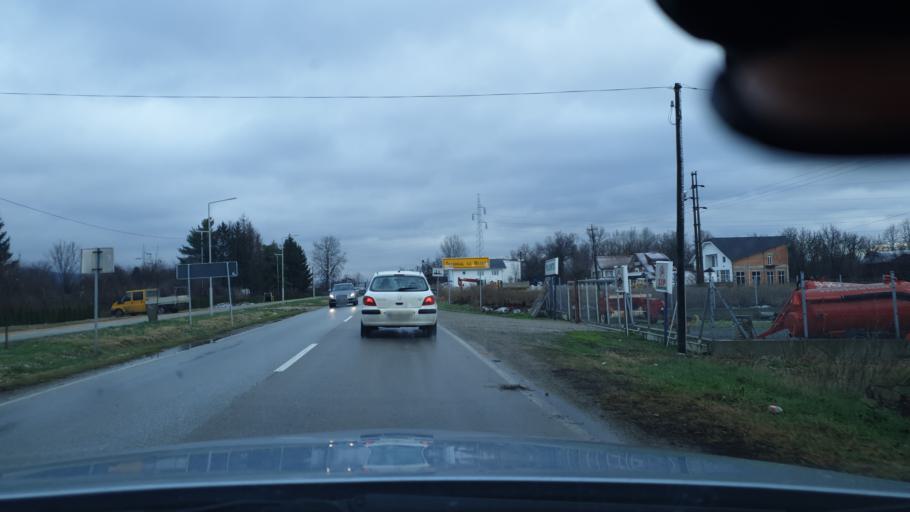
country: RS
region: Central Serbia
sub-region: Branicevski Okrug
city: Petrovac
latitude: 44.3956
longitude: 21.4044
